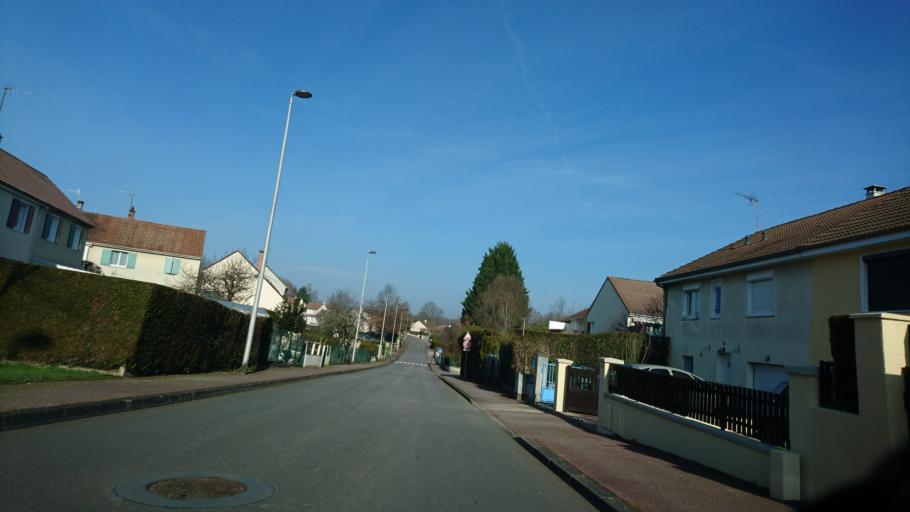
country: FR
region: Limousin
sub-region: Departement de la Haute-Vienne
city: Le Palais-sur-Vienne
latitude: 45.8795
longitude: 1.3035
